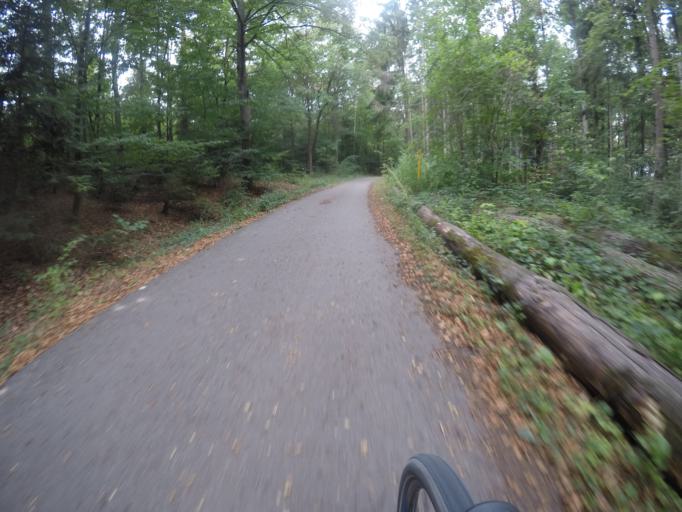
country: DE
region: Baden-Wuerttemberg
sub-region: Karlsruhe Region
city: Wurmberg
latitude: 48.8686
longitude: 8.8034
